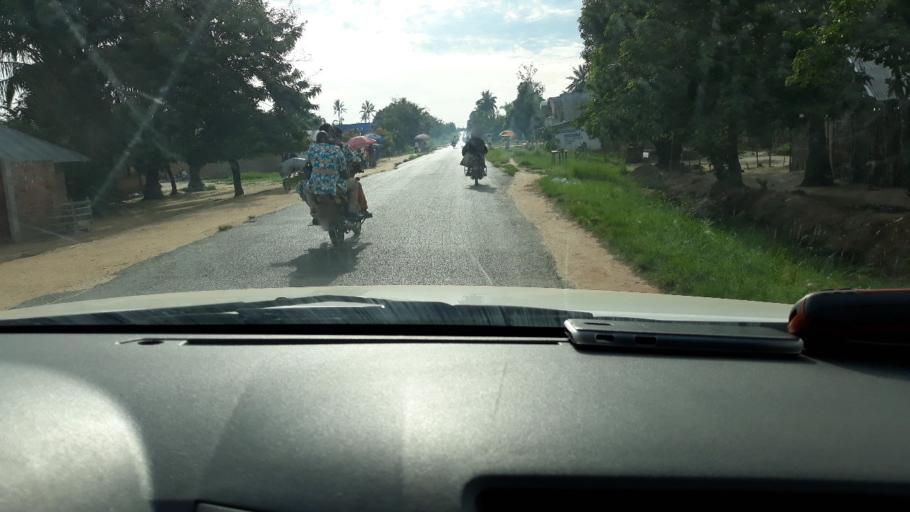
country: CD
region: Maniema
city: Kindu
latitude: -2.9521
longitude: 25.9418
